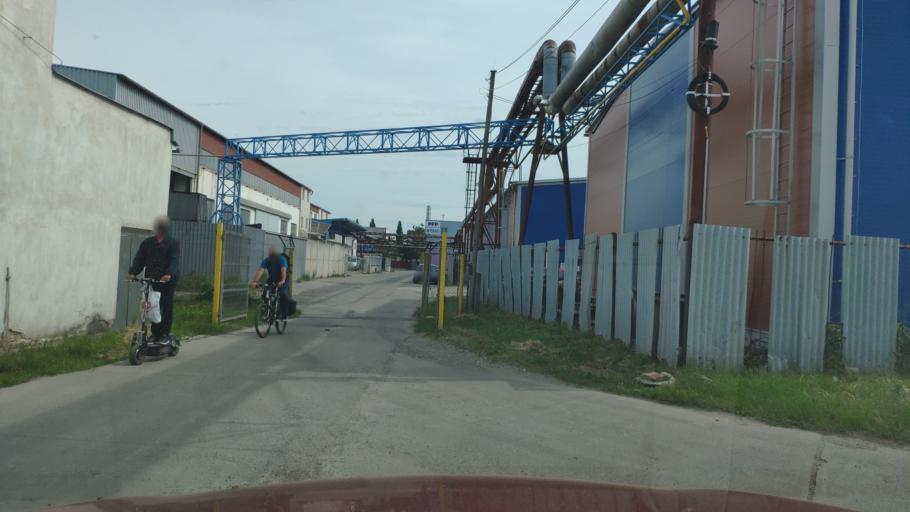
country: SK
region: Kosicky
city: Kosice
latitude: 48.6928
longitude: 21.2678
